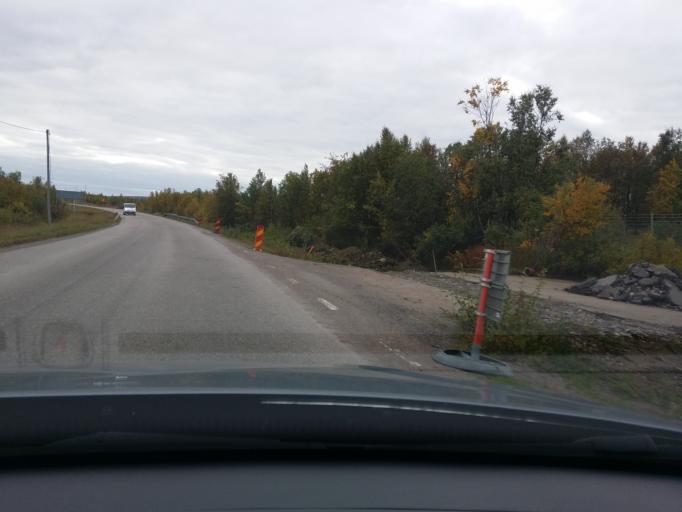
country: SE
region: Norrbotten
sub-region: Kiruna Kommun
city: Kiruna
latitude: 67.8435
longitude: 20.3490
